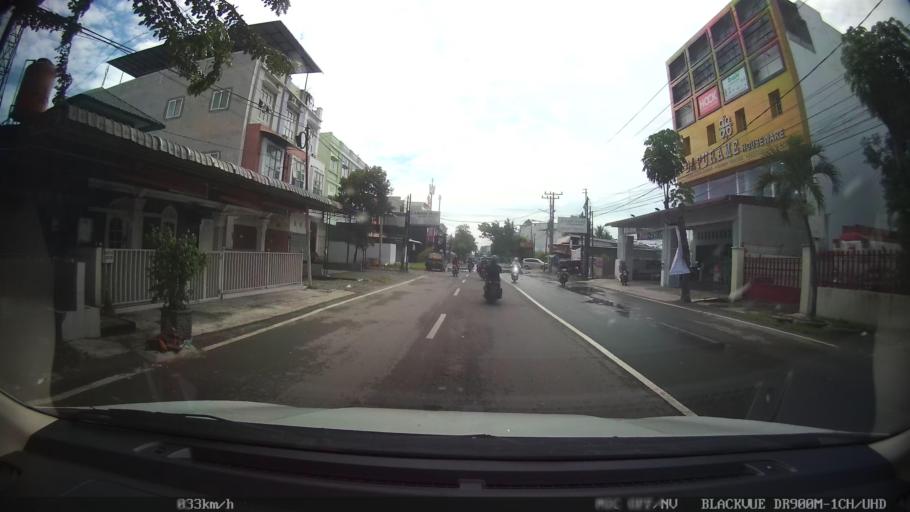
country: ID
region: North Sumatra
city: Medan
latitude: 3.6225
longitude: 98.7001
